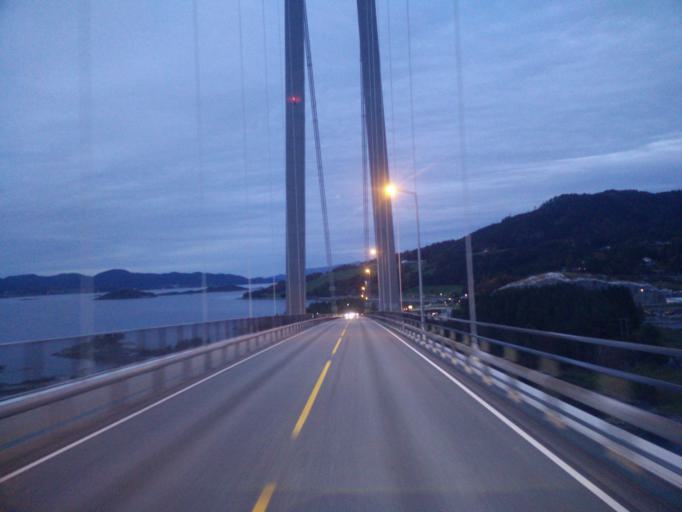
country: NO
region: More og Romsdal
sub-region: Kristiansund
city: Rensvik
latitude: 62.9728
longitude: 7.7818
